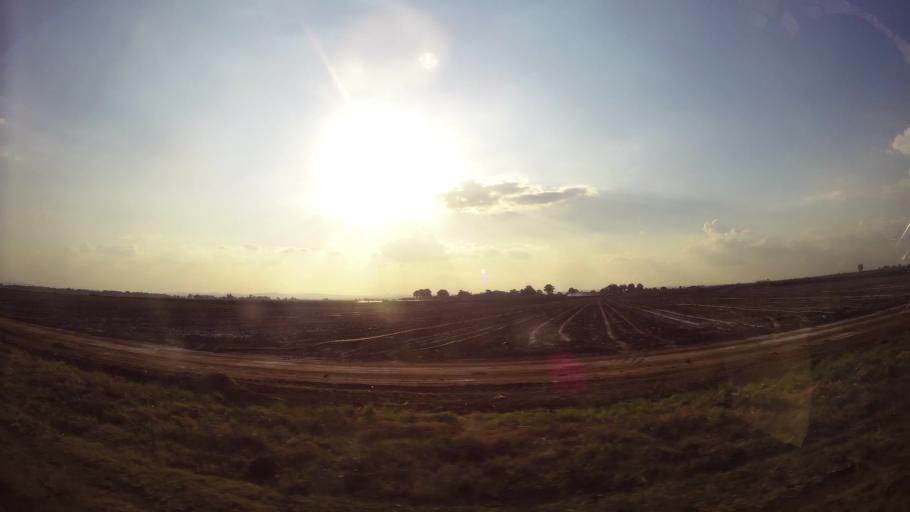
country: ZA
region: Gauteng
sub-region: Ekurhuleni Metropolitan Municipality
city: Germiston
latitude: -26.3244
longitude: 28.2427
